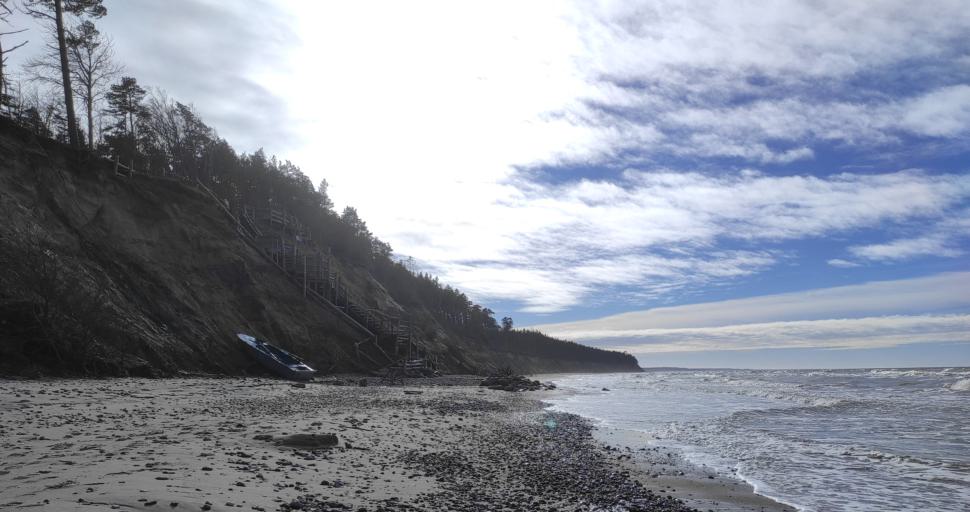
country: LV
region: Alsunga
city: Alsunga
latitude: 57.0296
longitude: 21.3972
